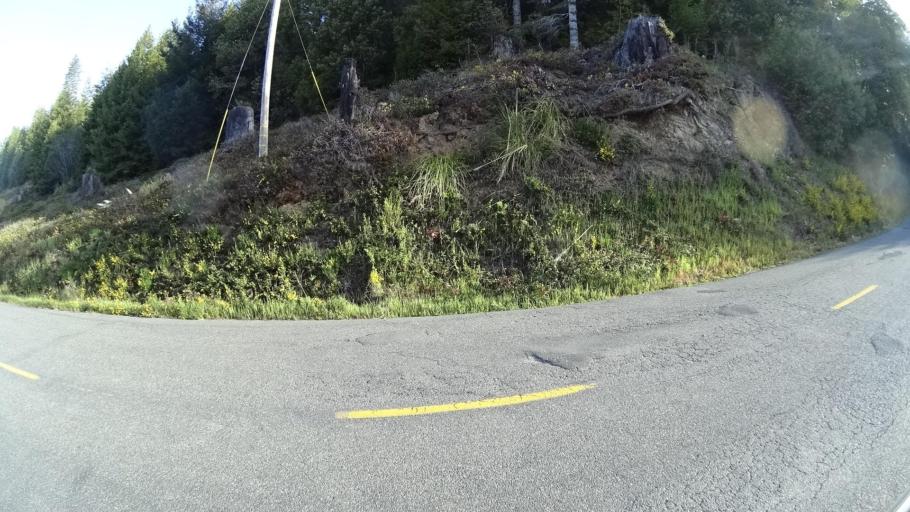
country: US
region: California
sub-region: Humboldt County
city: Bayside
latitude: 40.7595
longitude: -124.0078
